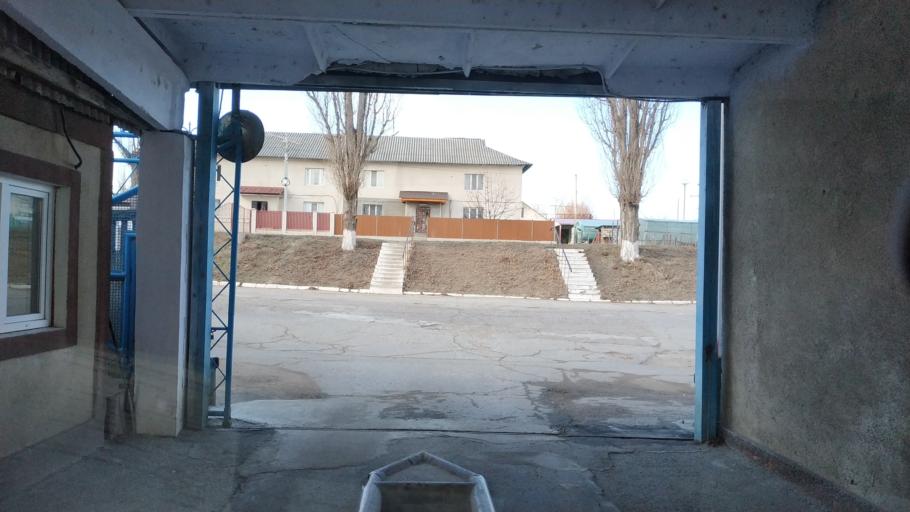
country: MD
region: Causeni
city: Causeni
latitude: 46.6589
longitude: 29.4213
